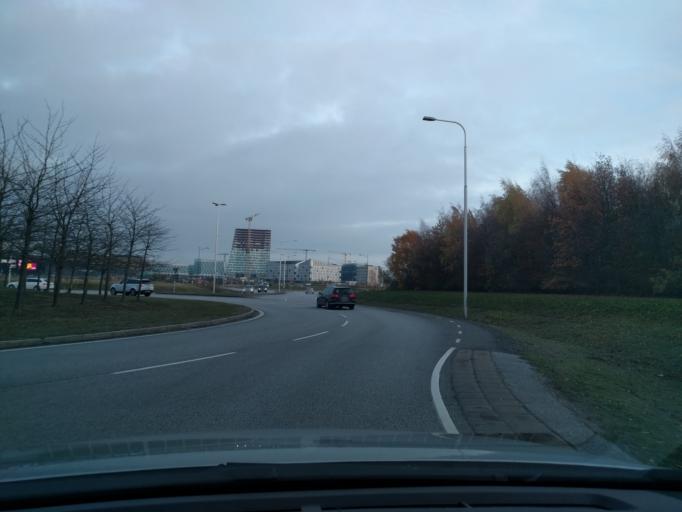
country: SE
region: Skane
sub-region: Malmo
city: Bunkeflostrand
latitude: 55.5604
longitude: 12.9668
